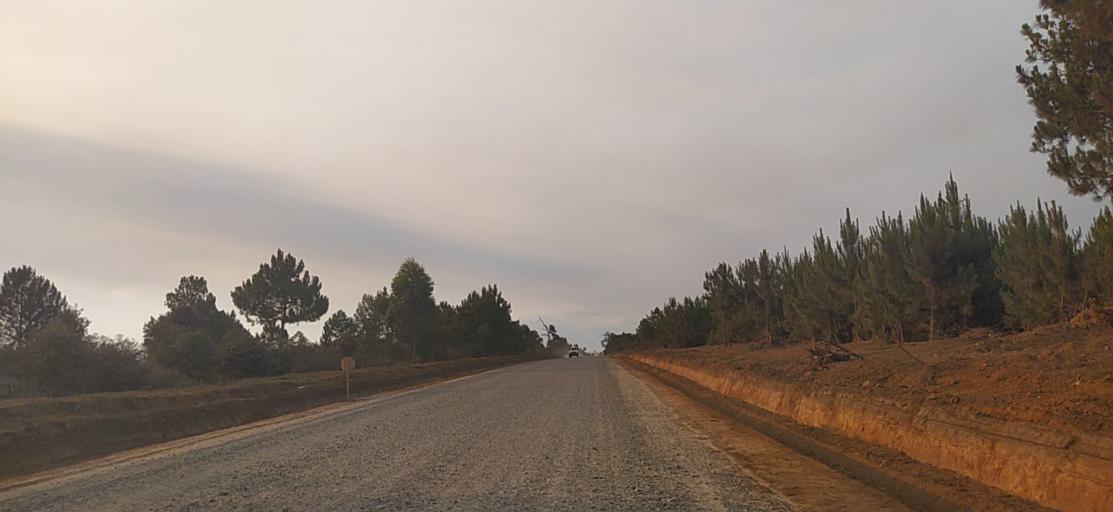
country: MG
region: Alaotra Mangoro
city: Moramanga
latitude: -18.5442
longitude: 48.2600
